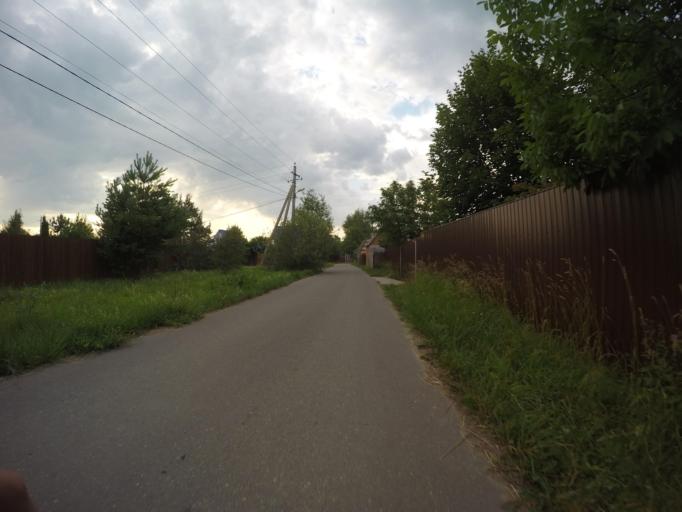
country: RU
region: Moskovskaya
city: Rechitsy
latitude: 55.5940
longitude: 38.5086
